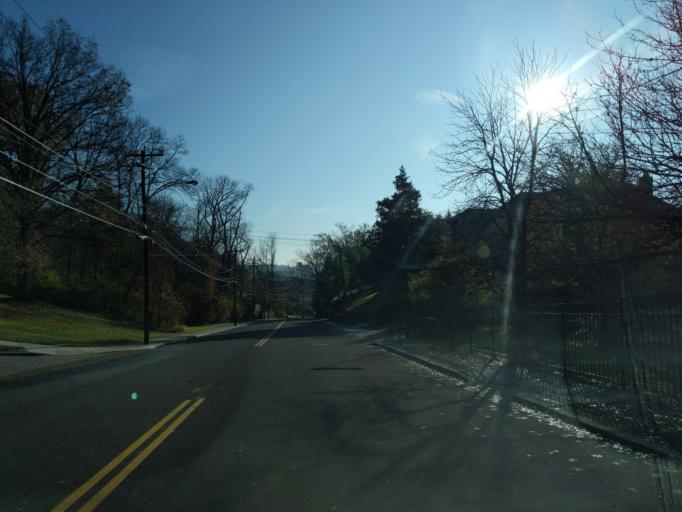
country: US
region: Kentucky
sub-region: Campbell County
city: Dayton
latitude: 39.1263
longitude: -84.4667
